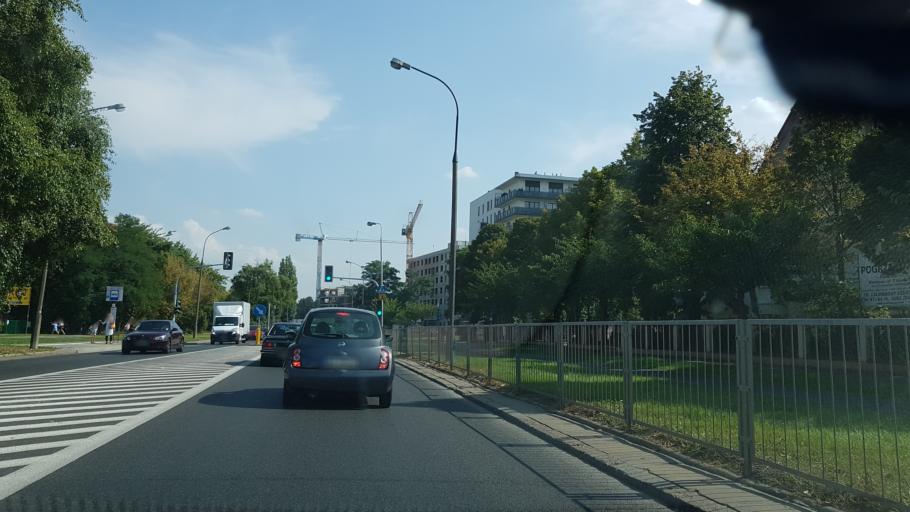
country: PL
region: Masovian Voivodeship
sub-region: Warszawa
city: Bielany
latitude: 52.2718
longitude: 20.9275
